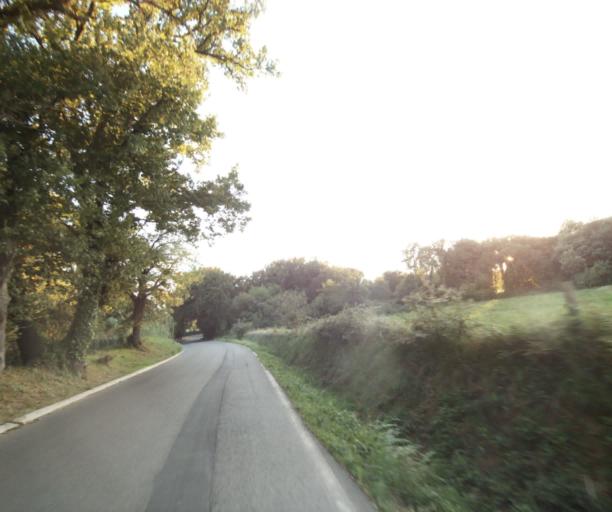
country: FR
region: Languedoc-Roussillon
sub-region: Departement des Pyrenees-Orientales
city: Argelers
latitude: 42.5722
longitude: 3.0141
